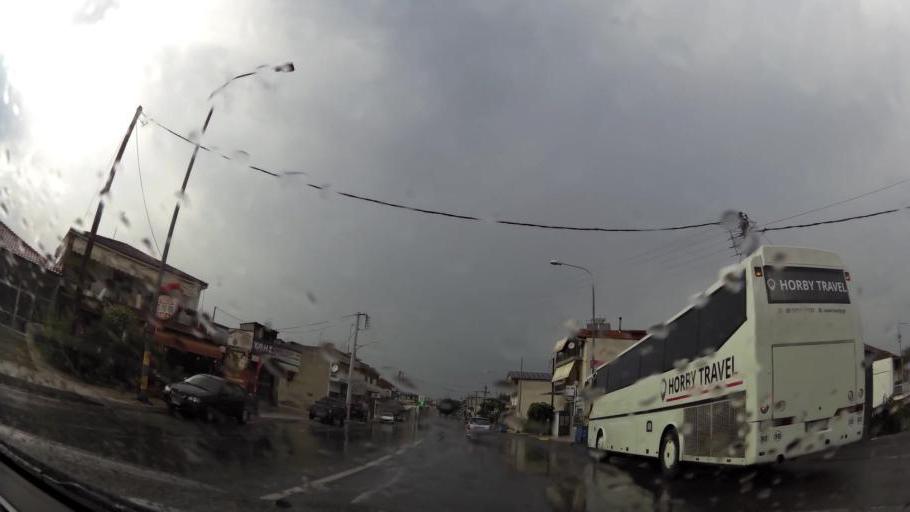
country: GR
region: Central Macedonia
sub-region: Nomos Imathias
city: Veroia
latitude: 40.5365
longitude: 22.2026
